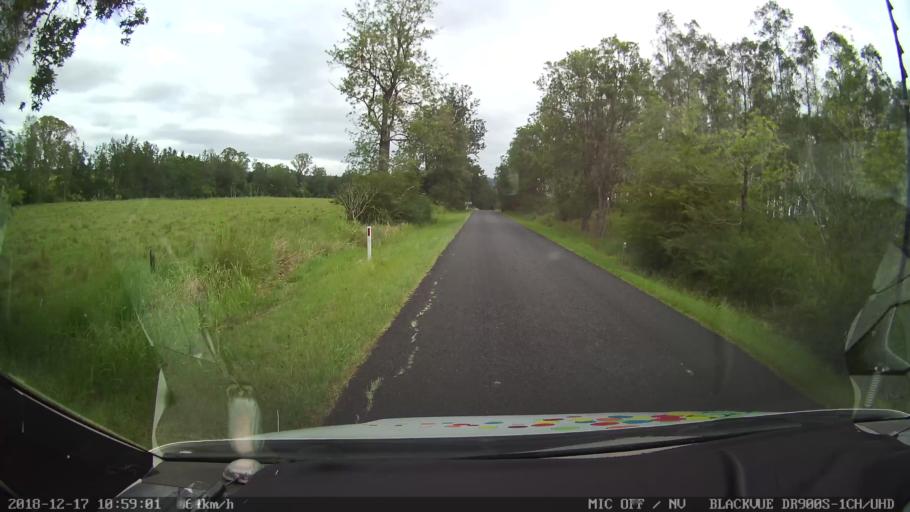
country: AU
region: New South Wales
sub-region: Richmond Valley
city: Casino
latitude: -28.8238
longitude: 152.6089
